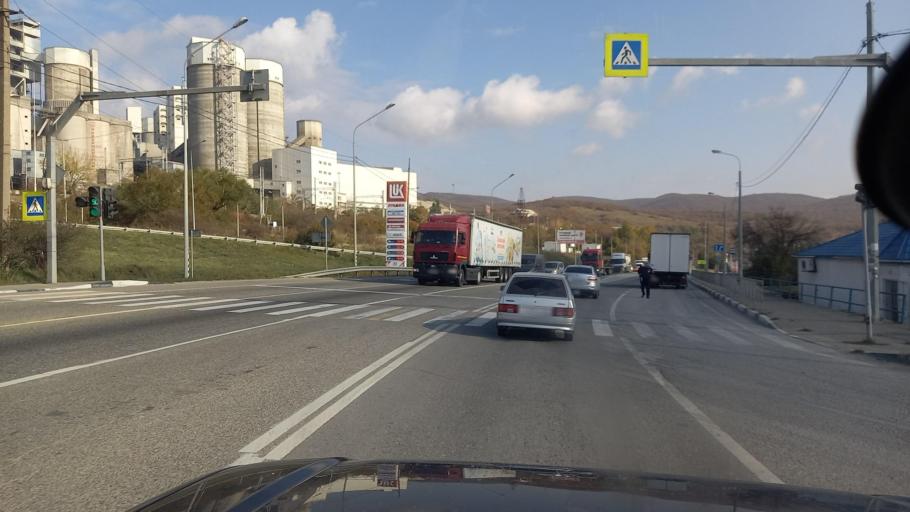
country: RU
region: Krasnodarskiy
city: Verkhnebakanskiy
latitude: 44.8413
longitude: 37.6696
